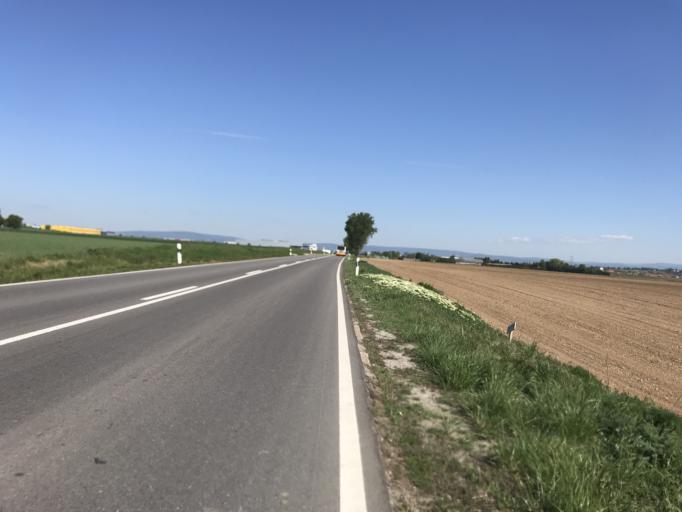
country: DE
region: Rheinland-Pfalz
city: Gau-Bischofsheim
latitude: 49.9382
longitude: 8.2644
